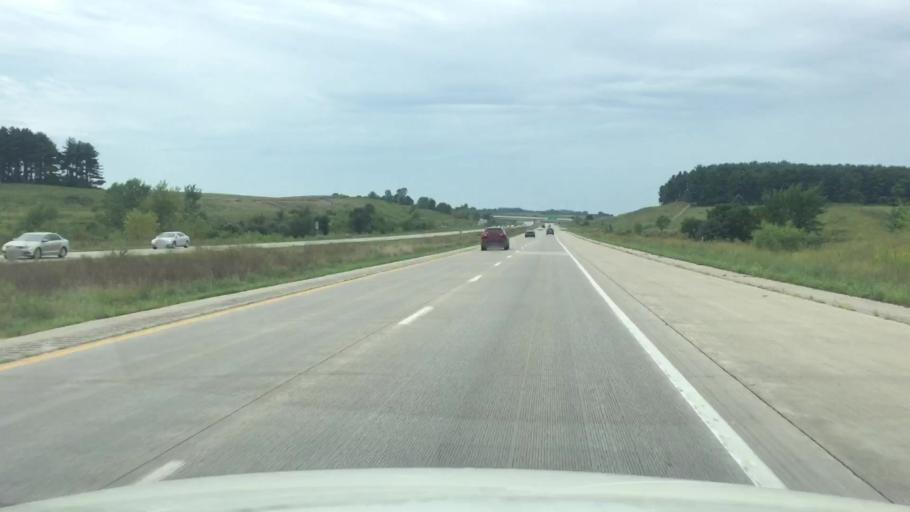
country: US
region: Iowa
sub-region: Polk County
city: West Des Moines
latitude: 41.5230
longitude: -93.7495
